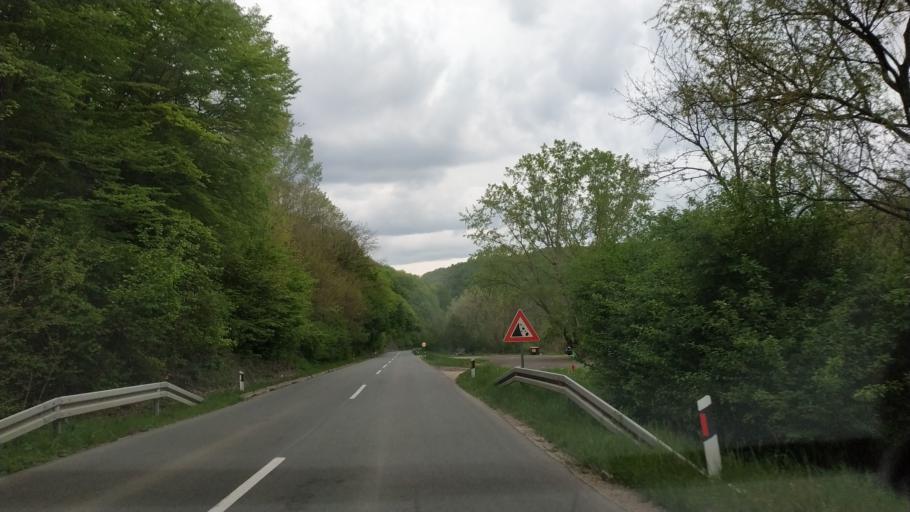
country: RS
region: Central Serbia
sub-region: Zajecarski Okrug
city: Soko Banja
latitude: 43.6520
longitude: 21.7572
